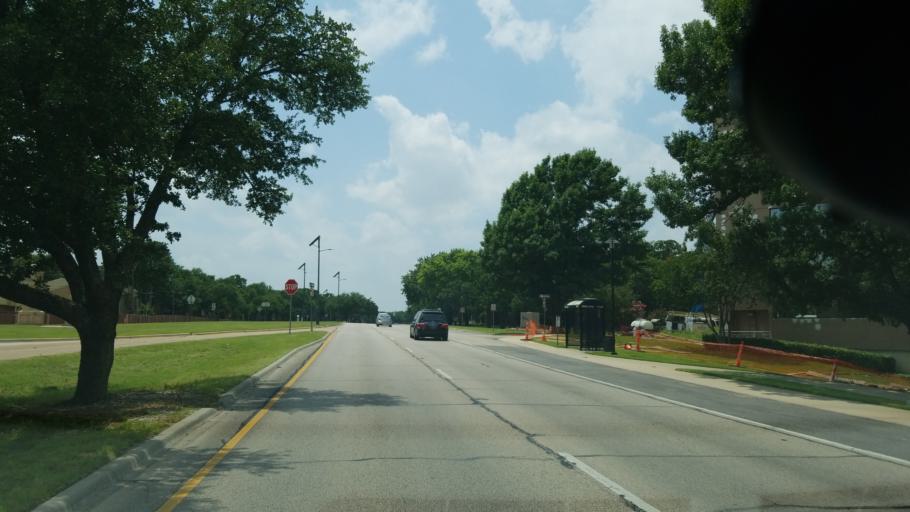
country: US
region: Texas
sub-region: Dallas County
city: Irving
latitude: 32.8138
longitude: -96.9533
